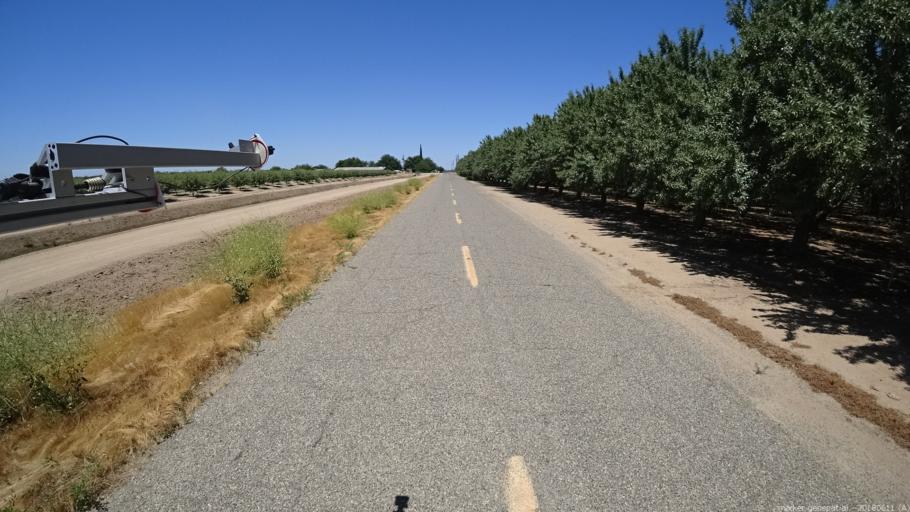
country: US
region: California
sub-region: Madera County
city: Fairmead
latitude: 37.0456
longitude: -120.2115
